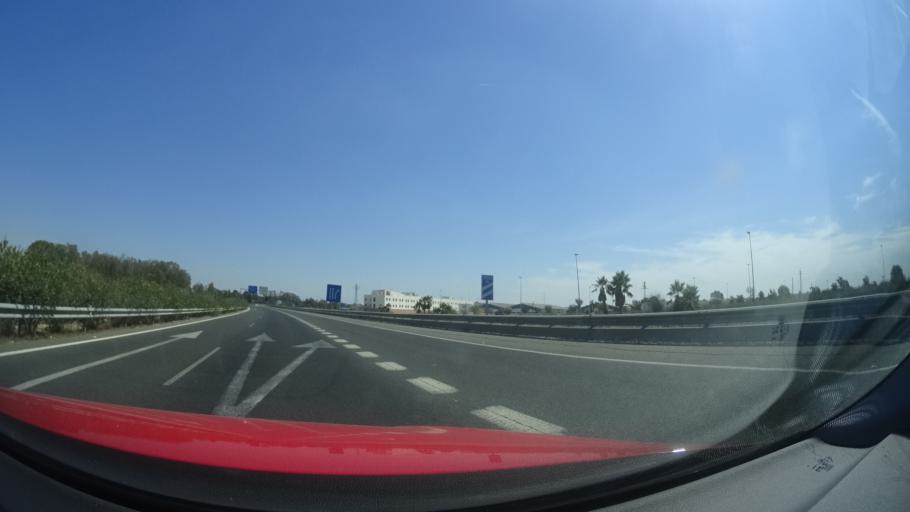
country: ES
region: Andalusia
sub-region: Provincia de Cadiz
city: Jerez de la Frontera
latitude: 36.7166
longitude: -6.1119
